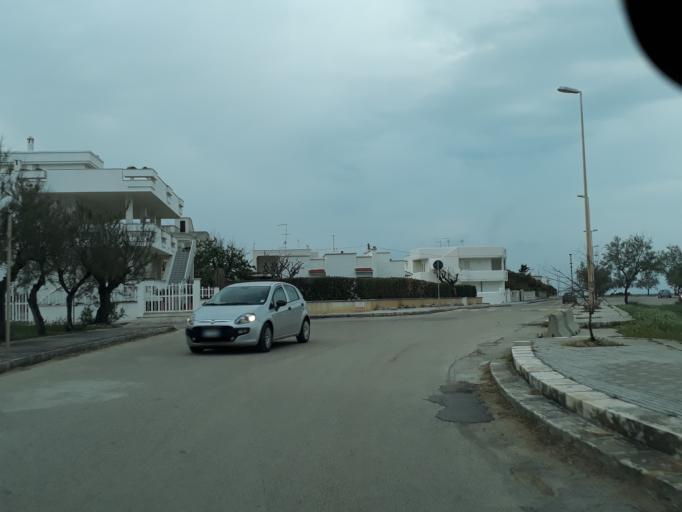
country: IT
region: Apulia
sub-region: Provincia di Brindisi
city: Carovigno
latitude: 40.7556
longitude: 17.7102
